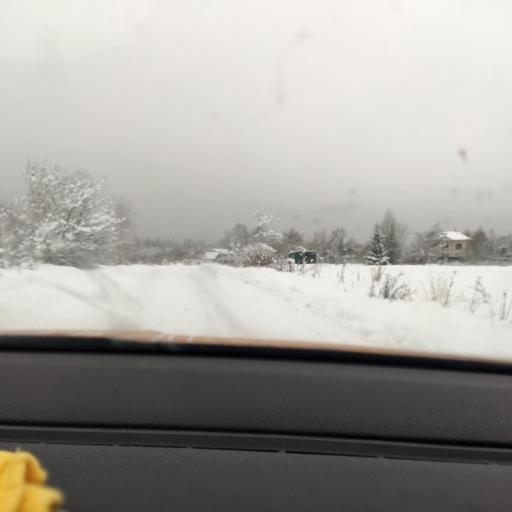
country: RU
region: Moskovskaya
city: Yershovo
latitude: 55.7891
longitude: 36.7773
